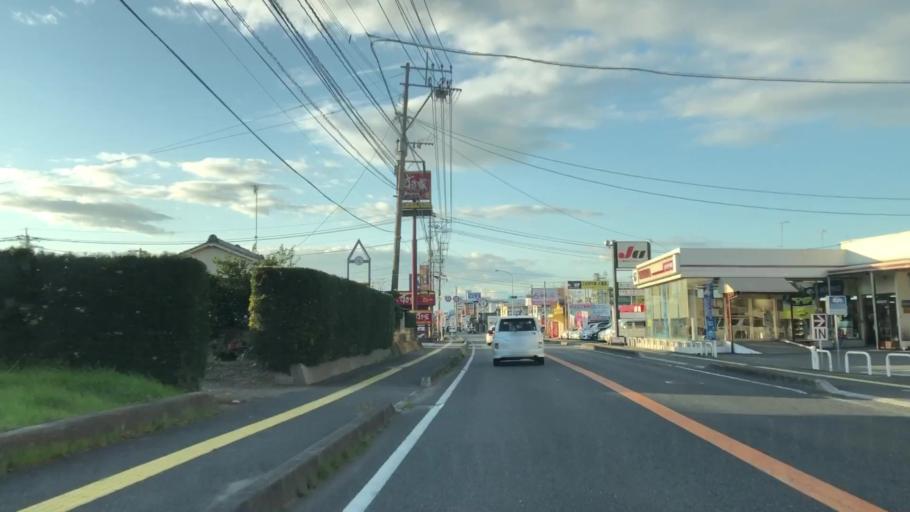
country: JP
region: Oita
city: Bungo-Takada-shi
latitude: 33.5297
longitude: 131.3372
